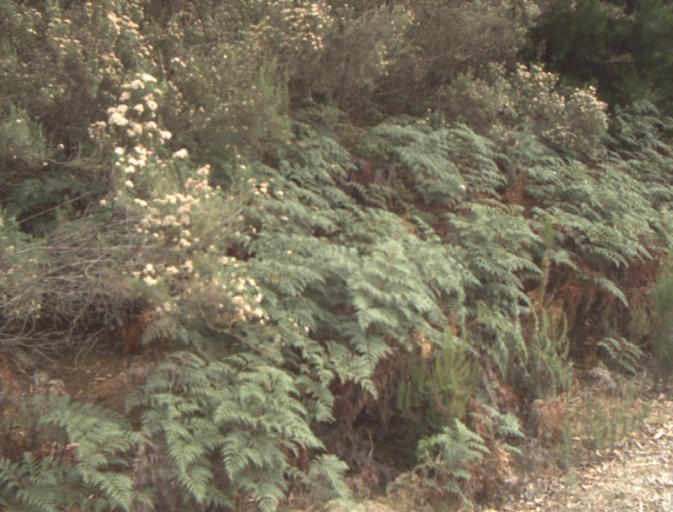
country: AU
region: Tasmania
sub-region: Launceston
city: Mayfield
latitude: -41.1533
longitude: 147.1727
